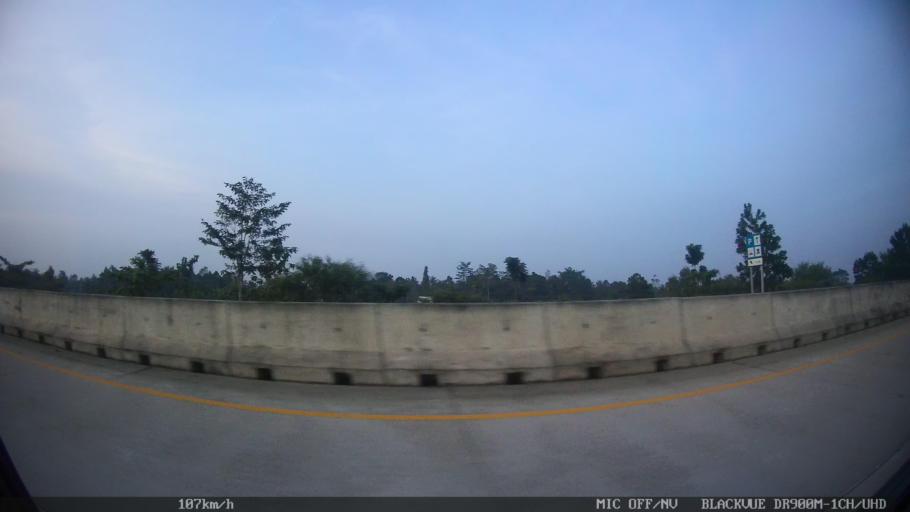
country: ID
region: Lampung
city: Pasuruan
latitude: -5.7174
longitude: 105.6591
